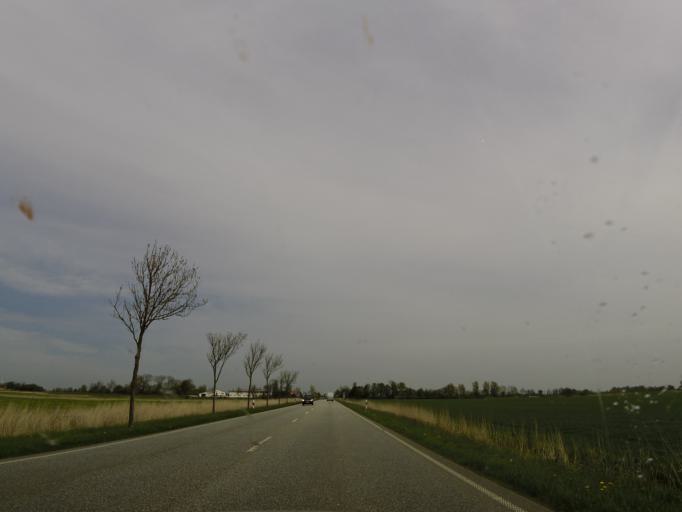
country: DE
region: Schleswig-Holstein
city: Koldenbuttel
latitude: 54.4092
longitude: 9.0388
